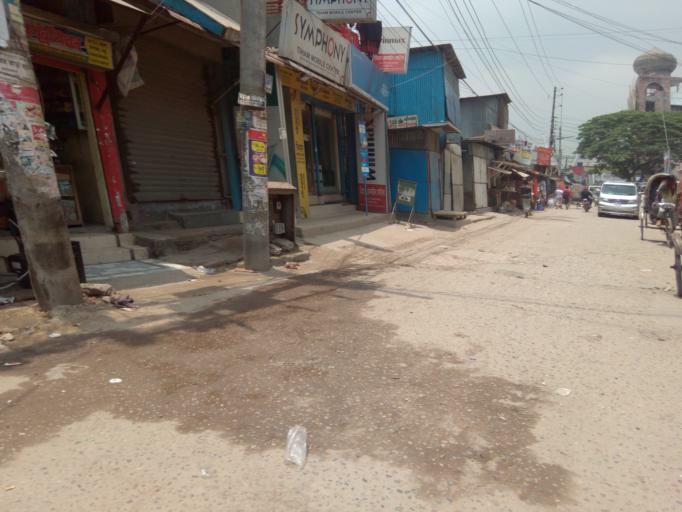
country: BD
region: Dhaka
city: Paltan
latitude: 23.7598
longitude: 90.4118
